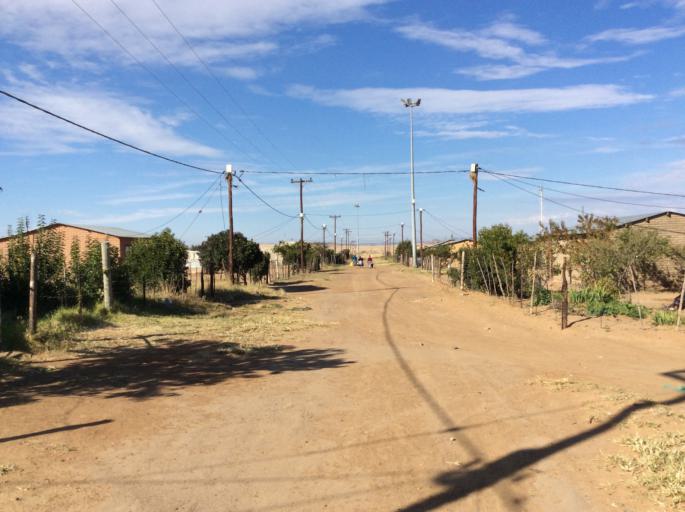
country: LS
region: Mafeteng
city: Mafeteng
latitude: -29.7117
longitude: 27.0152
